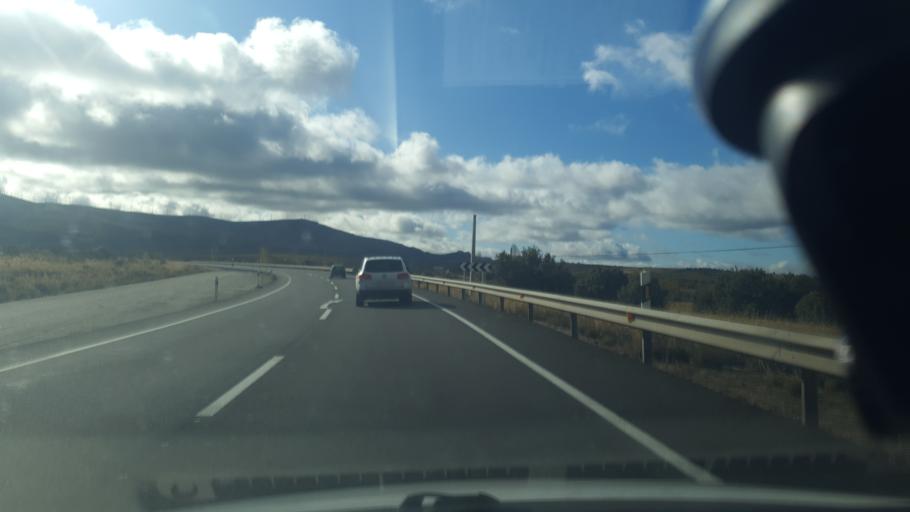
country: ES
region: Castille and Leon
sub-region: Provincia de Segovia
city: Villacastin
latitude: 40.7658
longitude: -4.4328
